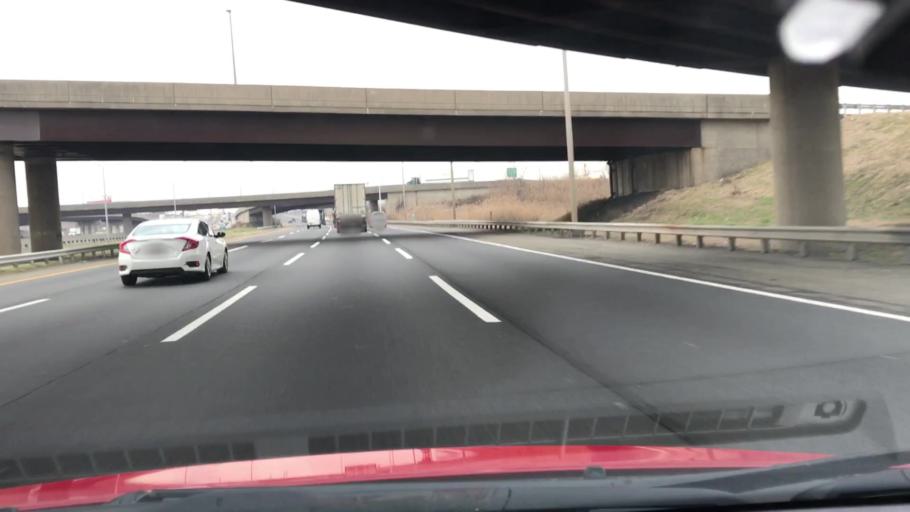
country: US
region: New Jersey
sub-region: Union County
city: Elizabeth
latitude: 40.6679
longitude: -74.1810
